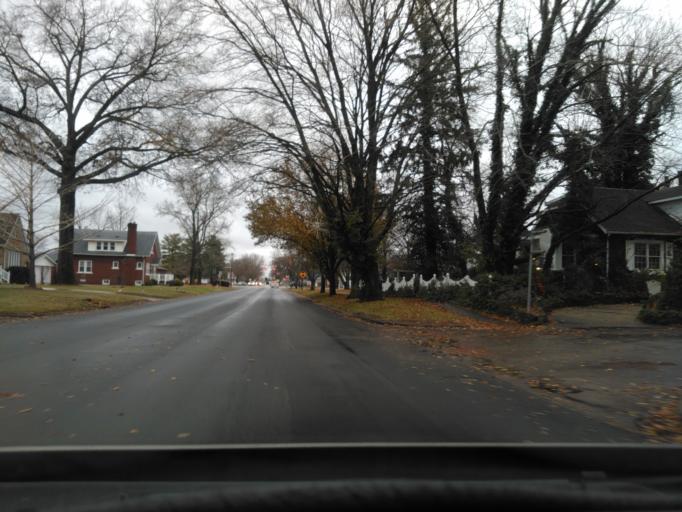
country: US
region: Illinois
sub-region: Effingham County
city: Altamont
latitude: 39.0568
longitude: -88.7480
